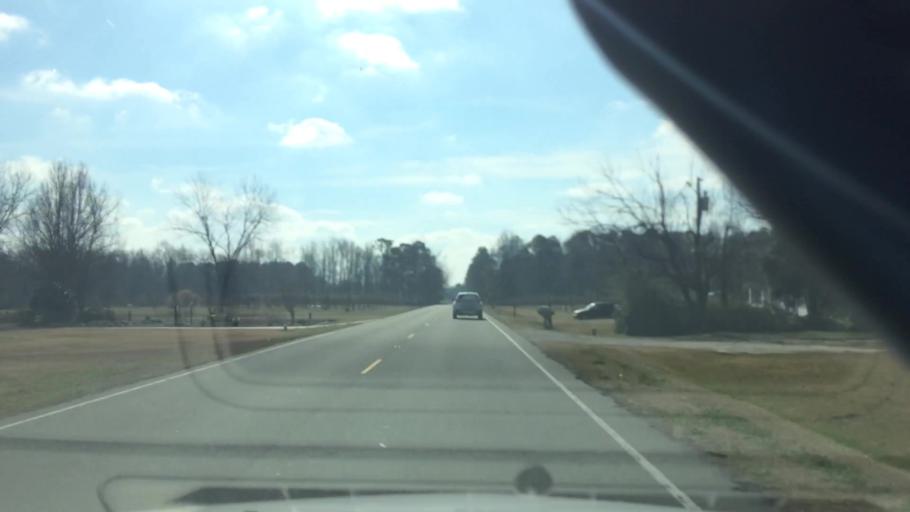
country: US
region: North Carolina
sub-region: Duplin County
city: Beulaville
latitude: 34.8655
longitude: -77.7938
